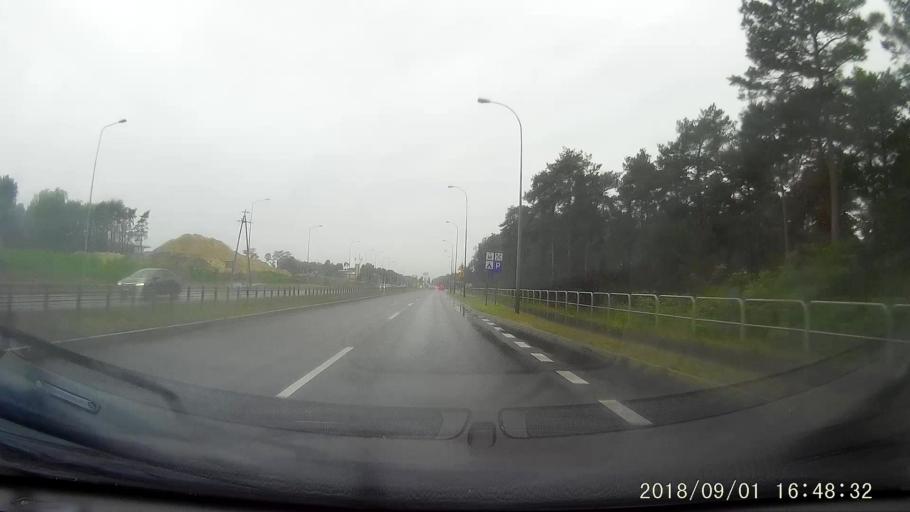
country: PL
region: Lubusz
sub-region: Zielona Gora
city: Zielona Gora
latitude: 51.9578
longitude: 15.5315
